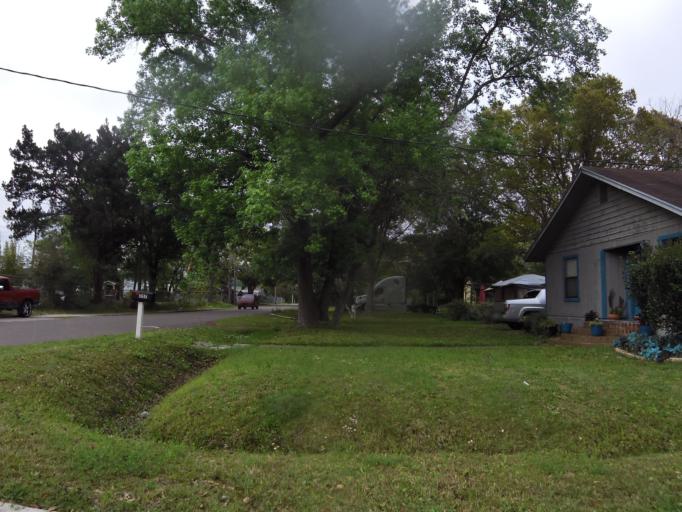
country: US
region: Florida
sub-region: Duval County
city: Jacksonville
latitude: 30.3234
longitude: -81.7173
